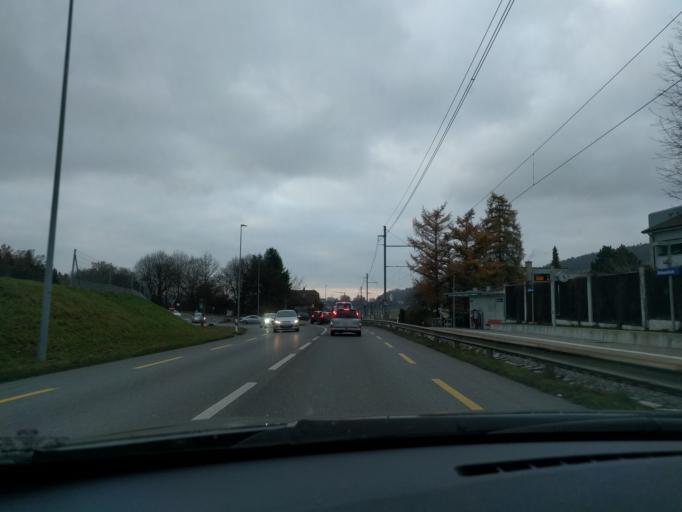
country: CH
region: Bern
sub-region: Bern-Mittelland District
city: Stettlen
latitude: 46.9306
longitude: 7.5268
